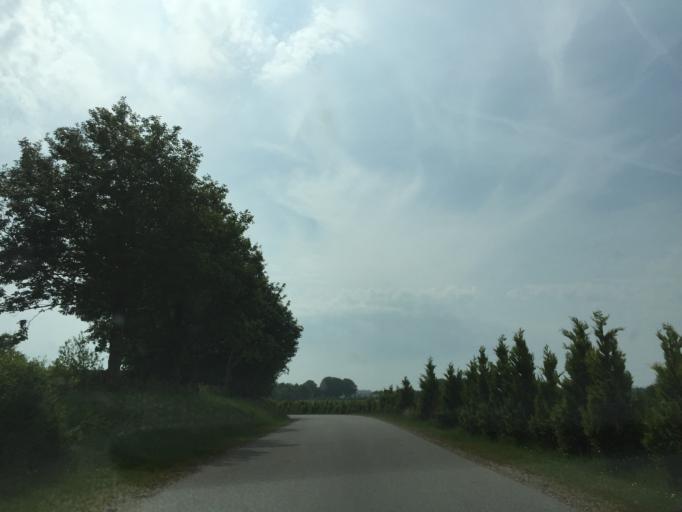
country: DK
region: Central Jutland
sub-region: Silkeborg Kommune
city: Virklund
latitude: 56.0908
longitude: 9.4707
